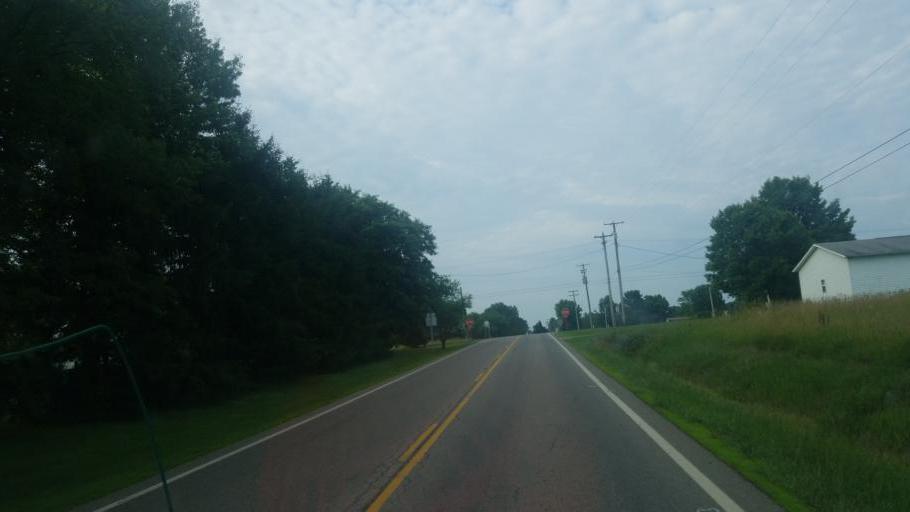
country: US
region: Ohio
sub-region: Ashland County
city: Ashland
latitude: 40.7736
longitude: -82.3066
